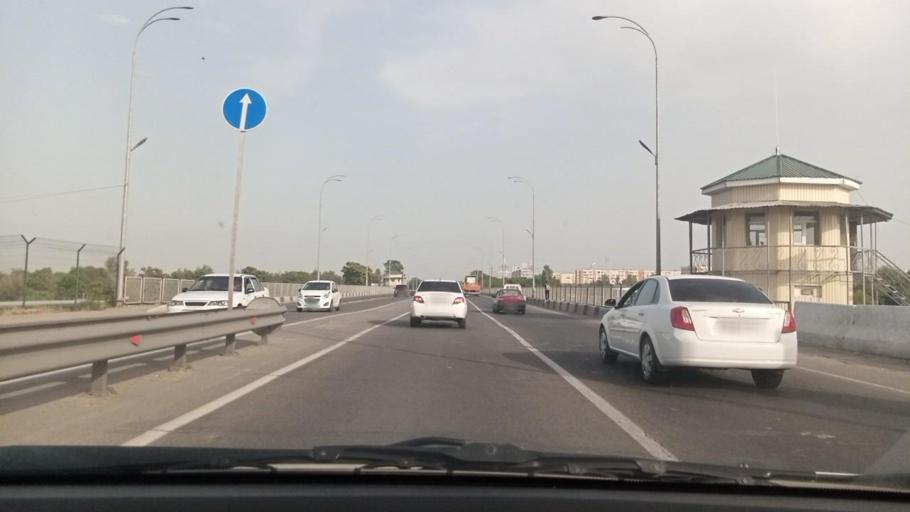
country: UZ
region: Toshkent Shahri
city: Bektemir
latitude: 41.2621
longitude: 69.3739
